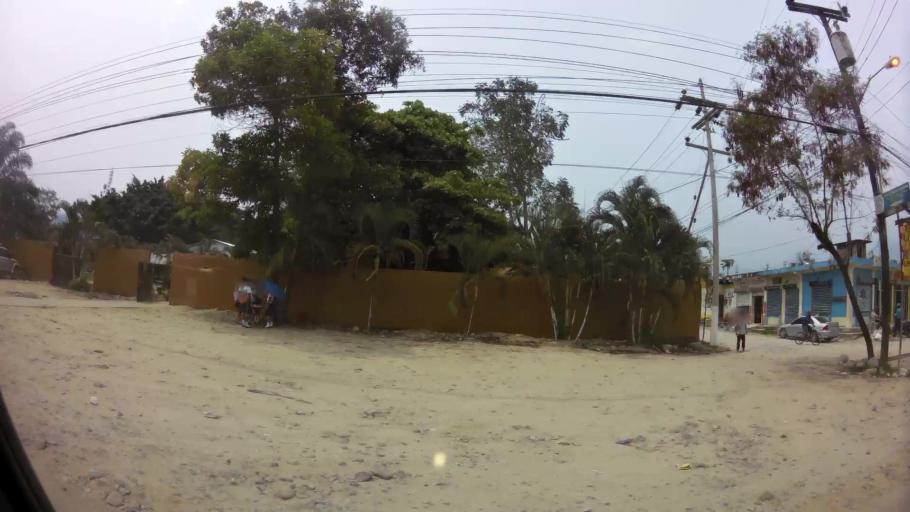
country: HN
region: Atlantida
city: San Juan Pueblo
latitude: 15.5990
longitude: -87.2086
